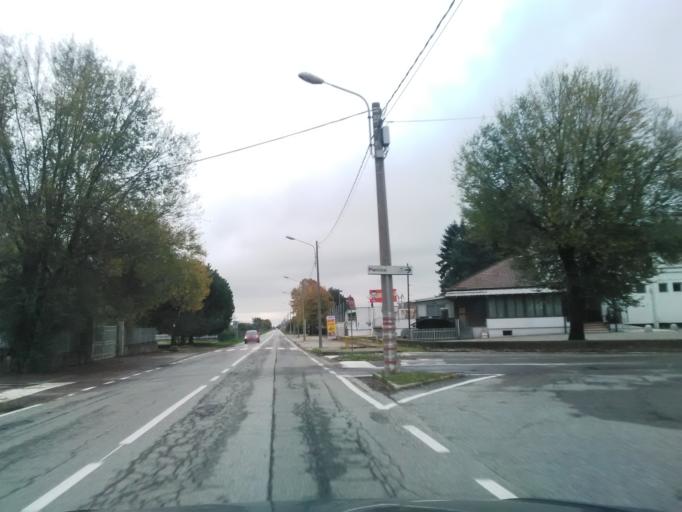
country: IT
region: Piedmont
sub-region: Provincia di Vercelli
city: Cigliano
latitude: 45.3106
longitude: 8.0297
